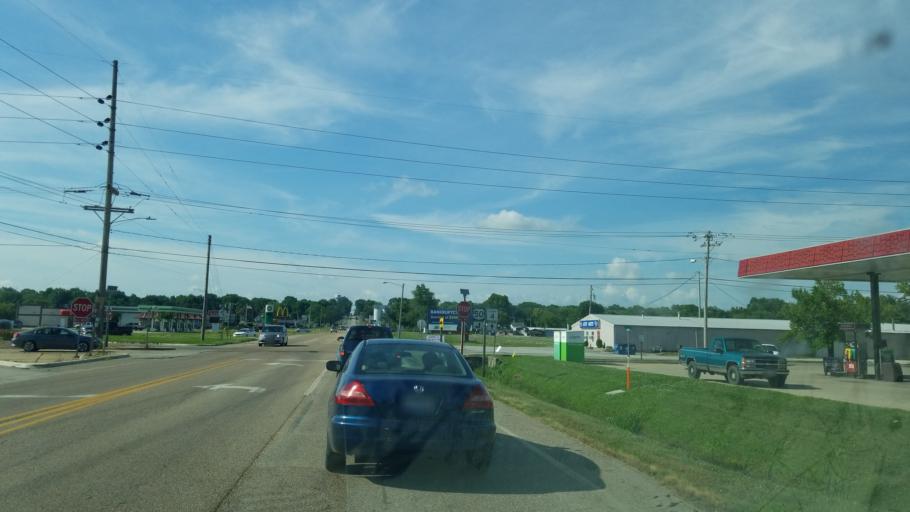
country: US
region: Illinois
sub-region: Saint Clair County
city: Lebanon
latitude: 38.5945
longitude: -89.8077
